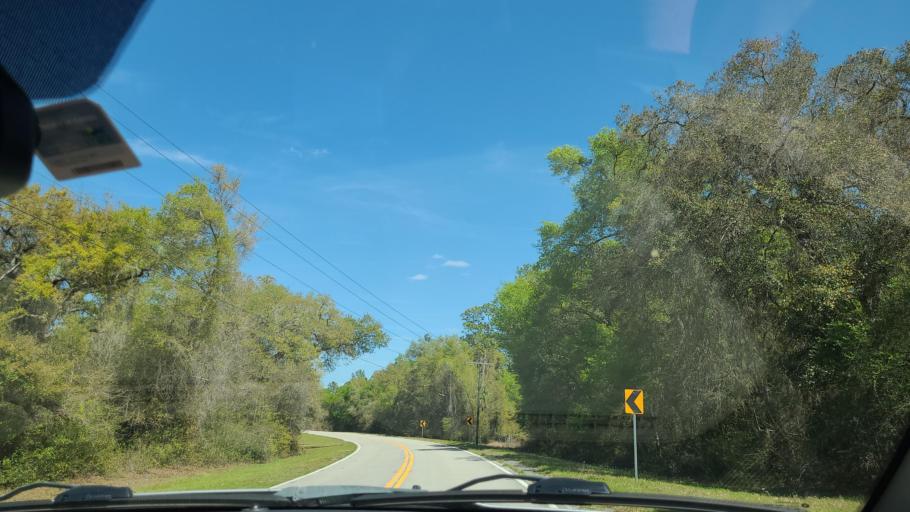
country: US
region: Florida
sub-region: Putnam County
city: Crescent City
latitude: 29.3782
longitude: -81.7738
